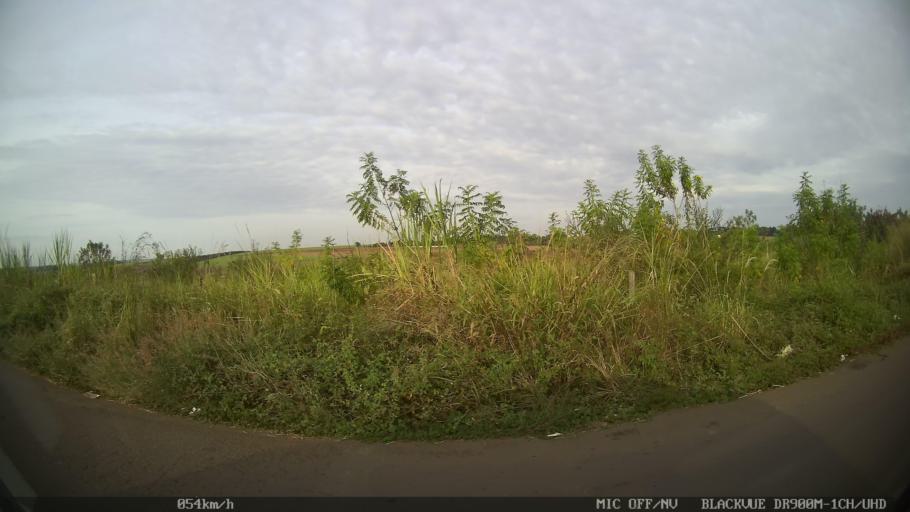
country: BR
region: Sao Paulo
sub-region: Piracicaba
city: Piracicaba
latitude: -22.7291
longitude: -47.5865
